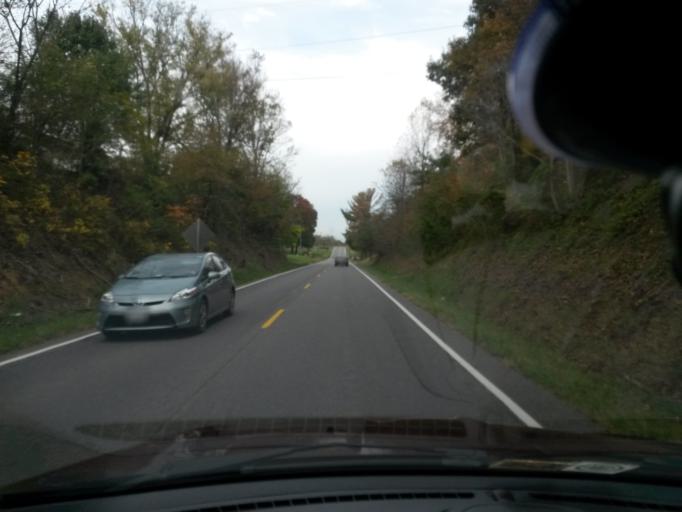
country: US
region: Virginia
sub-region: City of Roanoke
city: Cedar Bluff
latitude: 37.2309
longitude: -79.9058
